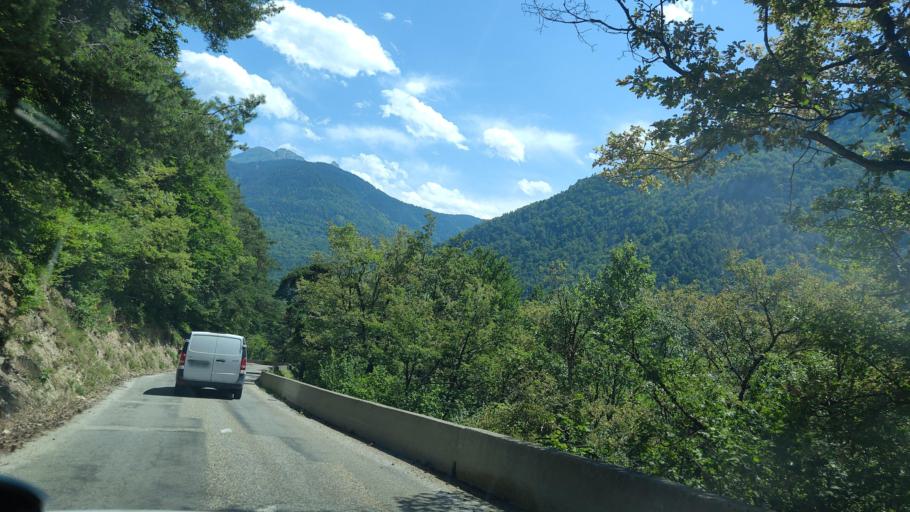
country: FR
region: Rhone-Alpes
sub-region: Departement de la Savoie
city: Salins-les-Thermes
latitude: 45.4624
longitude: 6.5523
